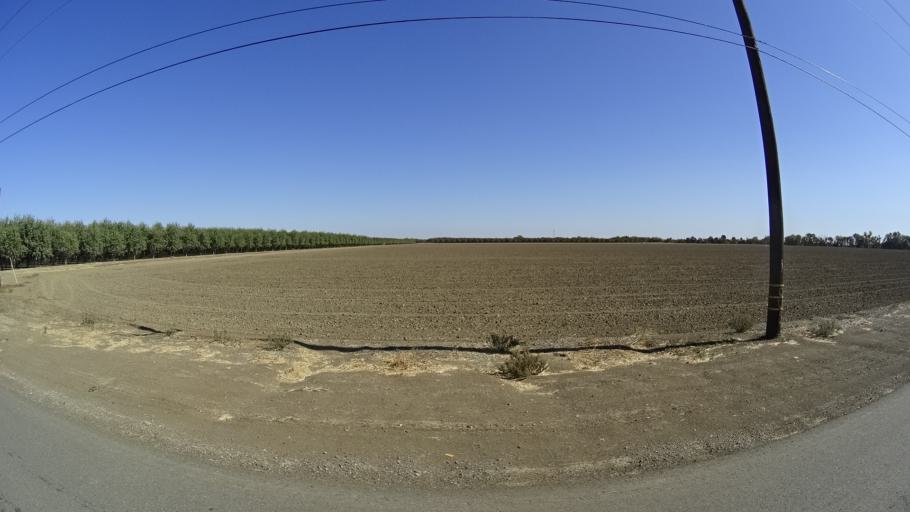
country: US
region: California
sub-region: Yolo County
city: Davis
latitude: 38.5974
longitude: -121.8036
